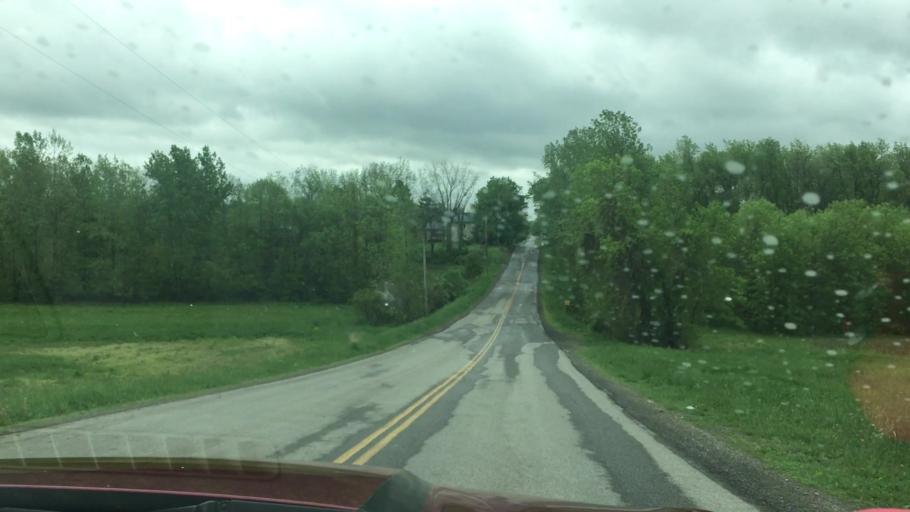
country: US
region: New York
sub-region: Genesee County
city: Batavia
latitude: 43.0830
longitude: -78.1395
